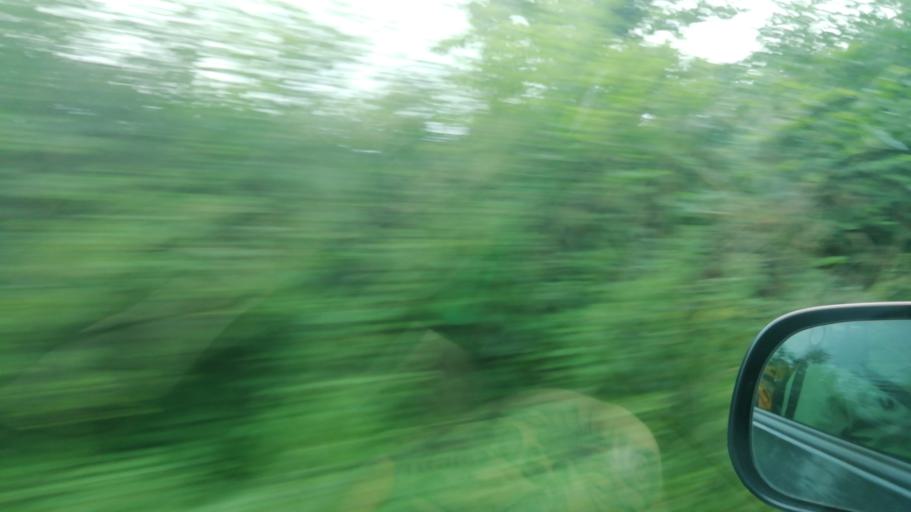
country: IE
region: Munster
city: Fethard
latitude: 52.5485
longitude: -7.6772
